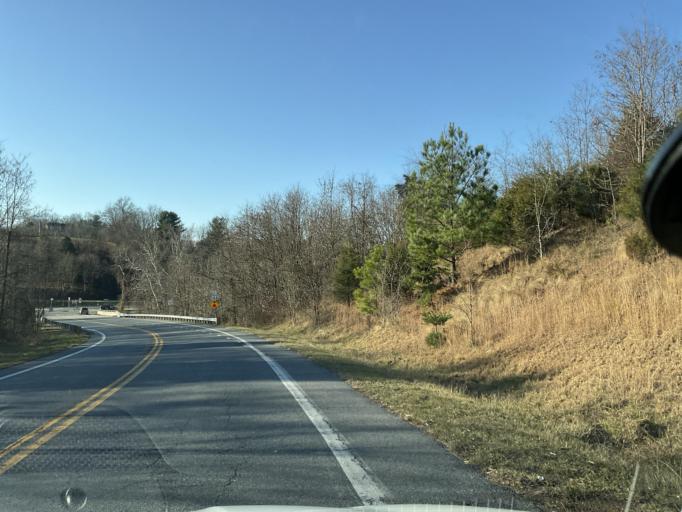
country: US
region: Maryland
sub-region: Frederick County
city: Spring Ridge
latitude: 39.3972
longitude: -77.3388
